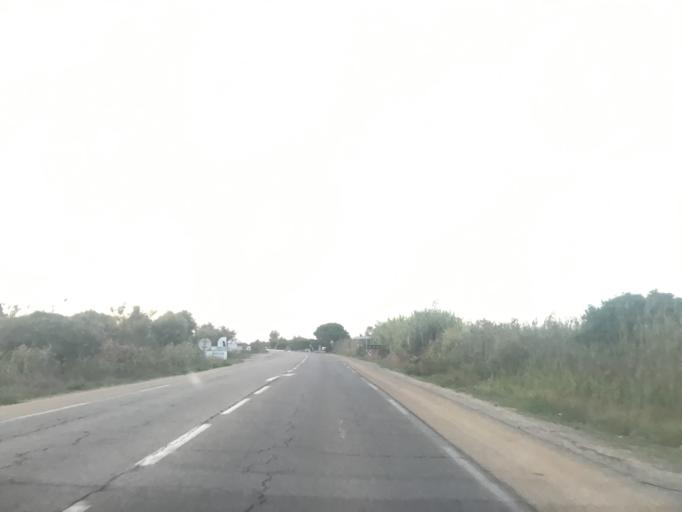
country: FR
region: Provence-Alpes-Cote d'Azur
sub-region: Departement des Bouches-du-Rhone
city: Saintes-Maries-de-la-Mer
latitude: 43.4850
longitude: 4.4044
